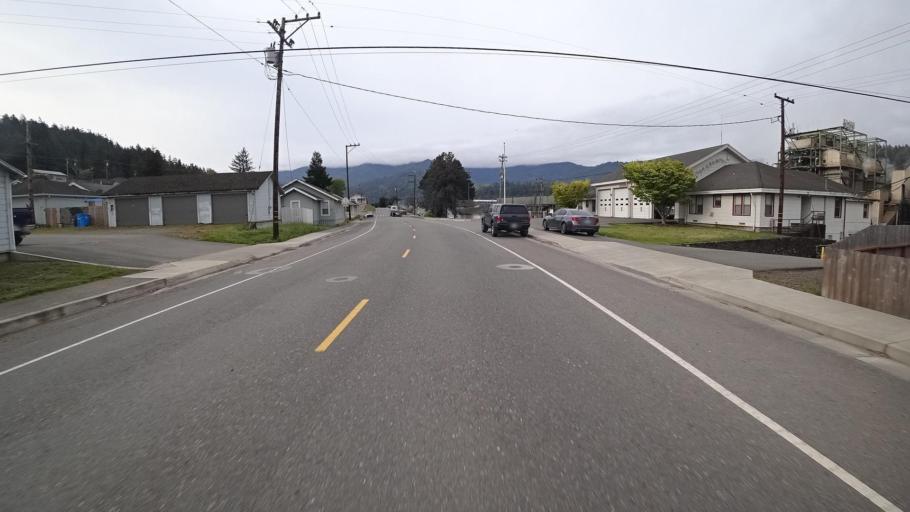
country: US
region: California
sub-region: Humboldt County
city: Rio Dell
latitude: 40.4818
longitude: -124.1031
